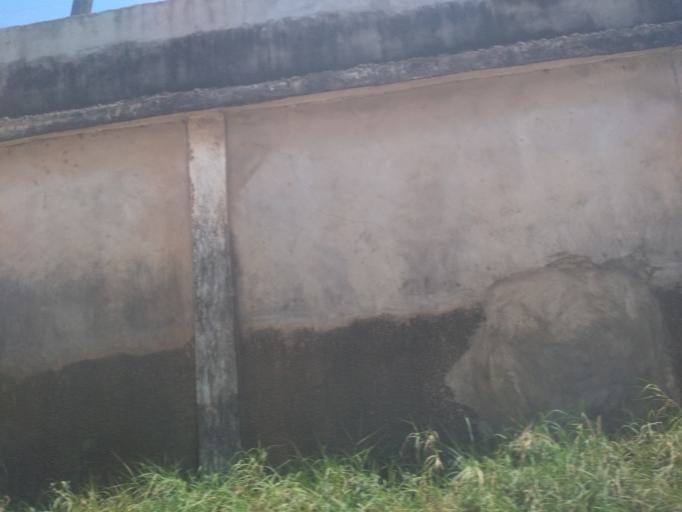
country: TZ
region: Dar es Salaam
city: Dar es Salaam
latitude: -6.8396
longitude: 39.2898
